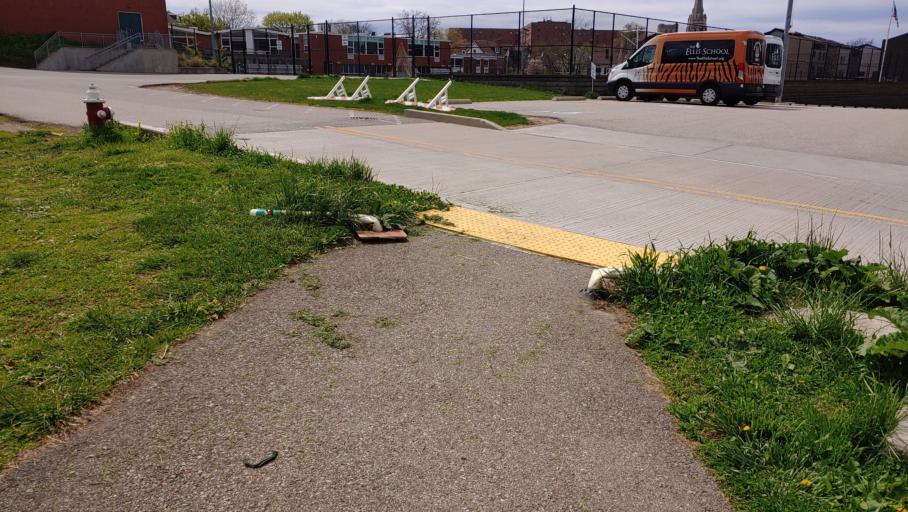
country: US
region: Pennsylvania
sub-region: Allegheny County
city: Bloomfield
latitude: 40.4550
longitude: -79.9165
